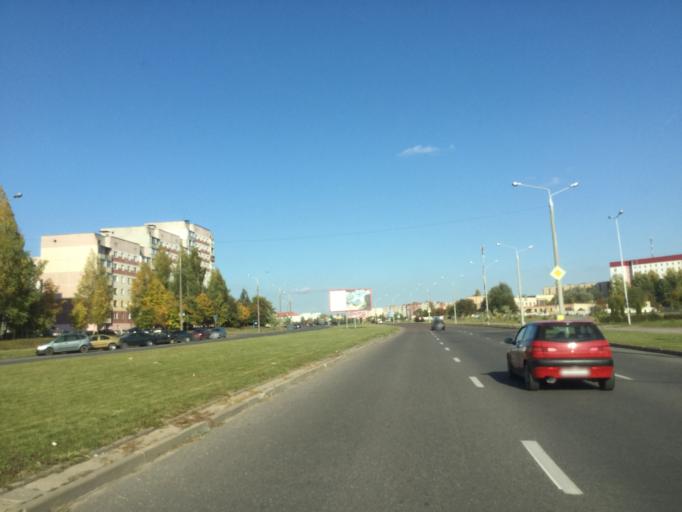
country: BY
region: Vitebsk
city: Vitebsk
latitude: 55.1577
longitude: 30.2161
